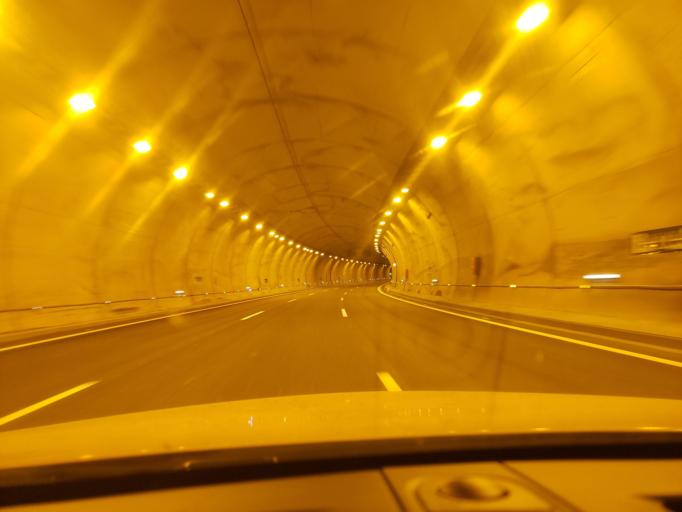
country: ES
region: Andalusia
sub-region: Provincia de Jaen
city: Santa Elena
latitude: 38.3837
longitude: -3.5061
